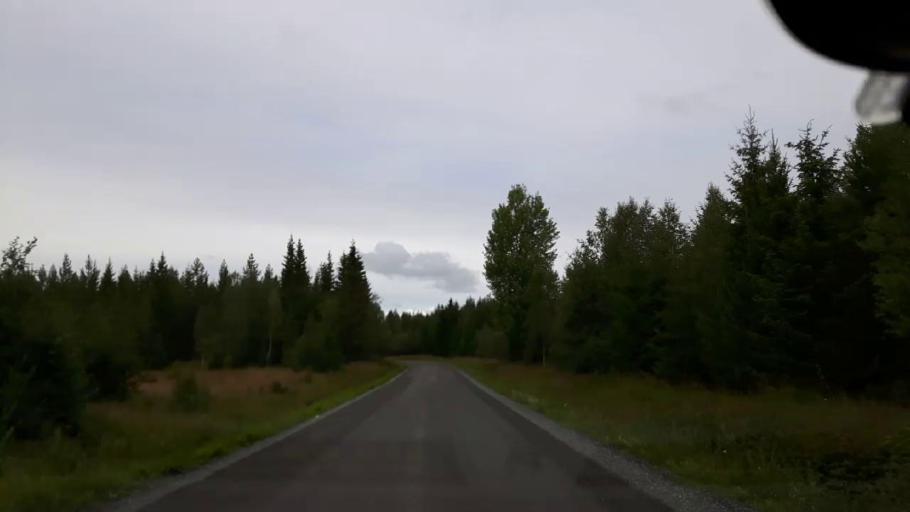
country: SE
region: Jaemtland
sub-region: Krokoms Kommun
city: Krokom
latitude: 63.3181
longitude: 14.3107
